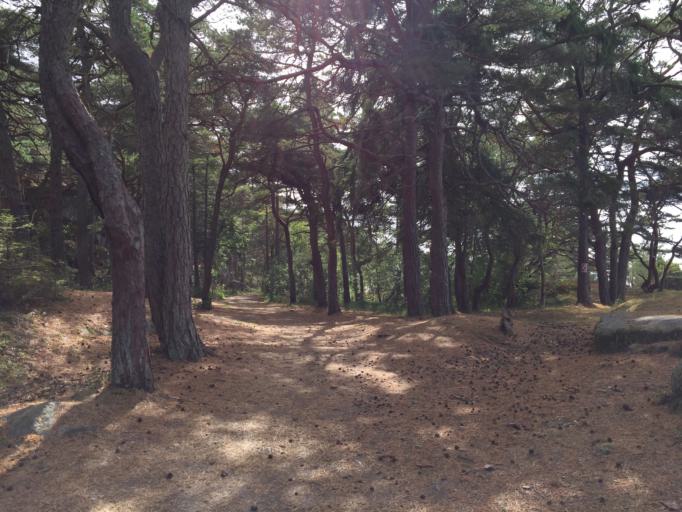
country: NO
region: Ostfold
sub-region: Hvaler
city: Skjaerhalden
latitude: 59.0238
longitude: 11.0191
